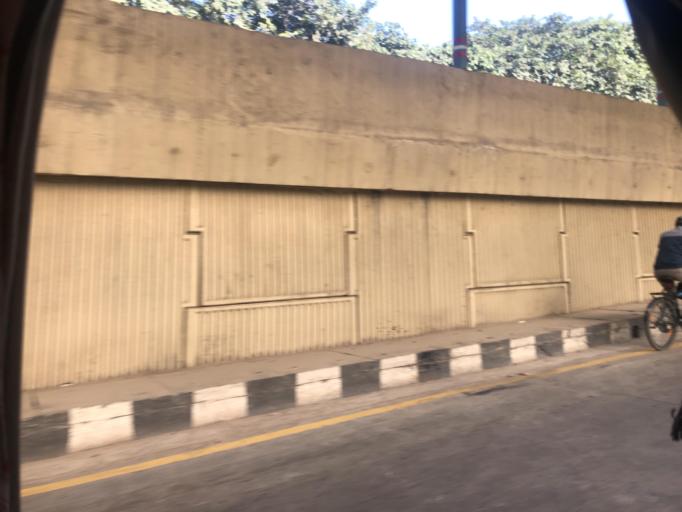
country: IN
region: Haryana
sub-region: Gurgaon
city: Gurgaon
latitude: 28.4671
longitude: 77.0600
